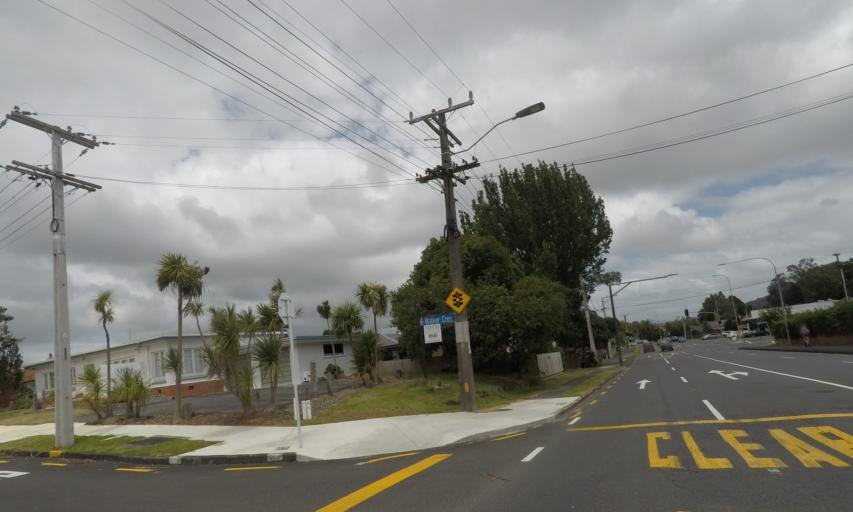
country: NZ
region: Northland
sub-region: Whangarei
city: Whangarei
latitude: -35.6976
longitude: 174.3125
